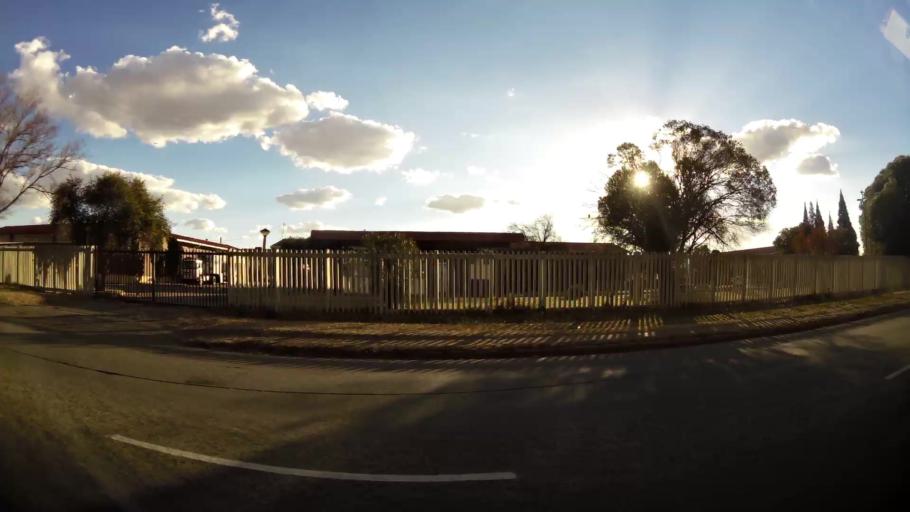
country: ZA
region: North-West
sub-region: Dr Kenneth Kaunda District Municipality
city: Potchefstroom
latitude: -26.7353
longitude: 27.0837
